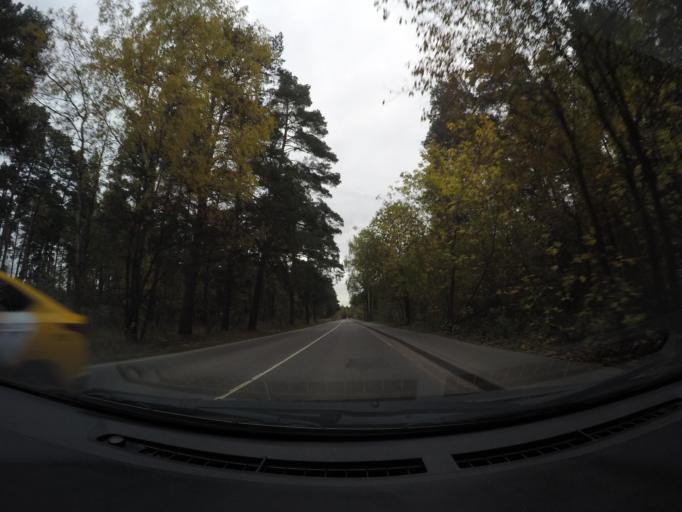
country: RU
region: Moskovskaya
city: Vishnyakovskiye Dachi
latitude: 55.8059
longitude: 38.1154
